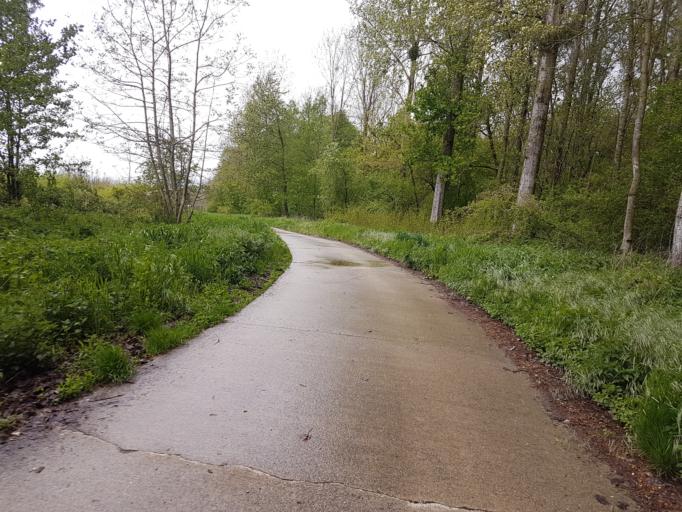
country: CH
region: Vaud
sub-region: Jura-Nord vaudois District
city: Chavornay
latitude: 46.7406
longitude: 6.5916
